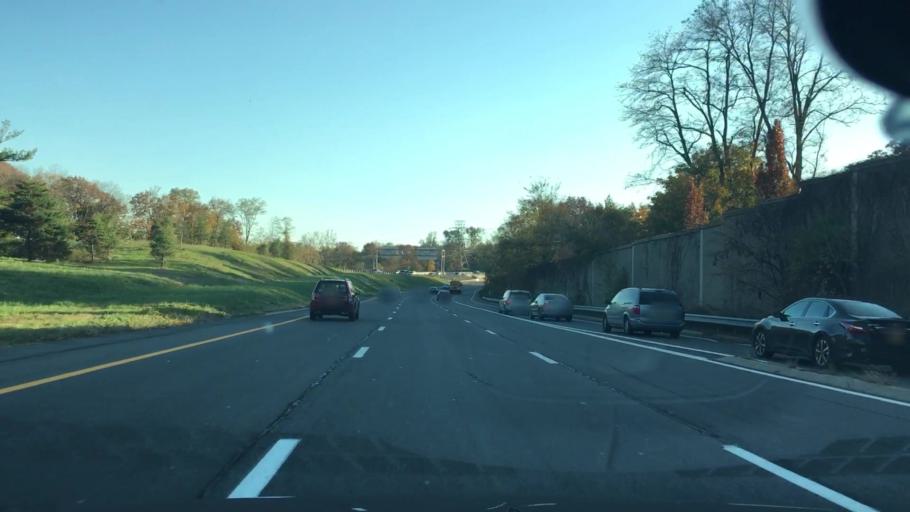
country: US
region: New York
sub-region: Westchester County
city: Elmsford
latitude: 41.0535
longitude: -73.8105
